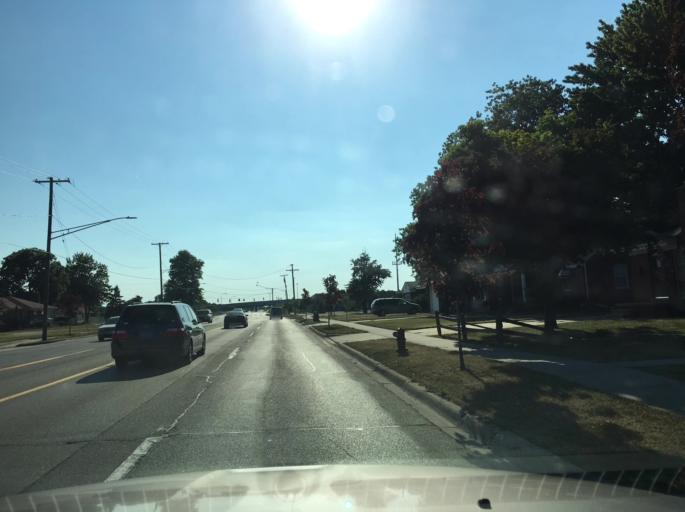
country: US
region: Michigan
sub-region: Macomb County
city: Roseville
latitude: 42.4954
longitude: -82.9133
